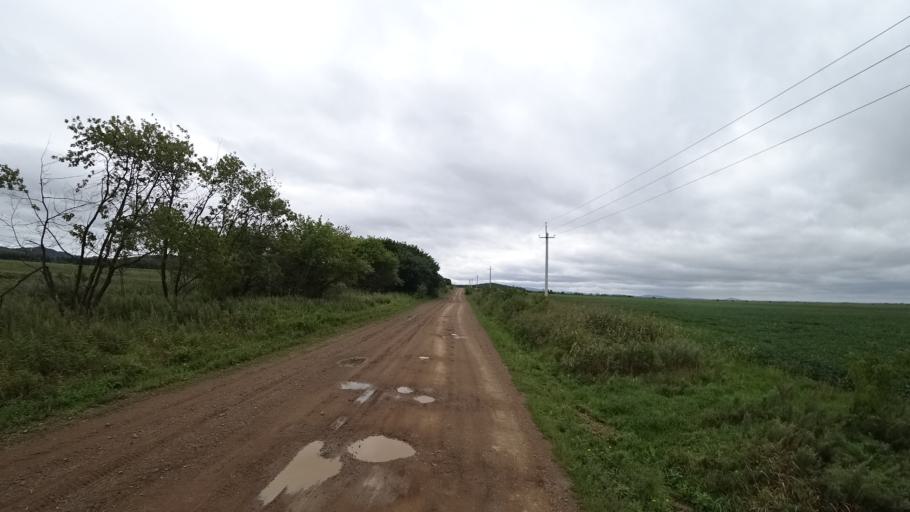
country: RU
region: Primorskiy
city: Chernigovka
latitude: 44.4873
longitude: 132.5730
